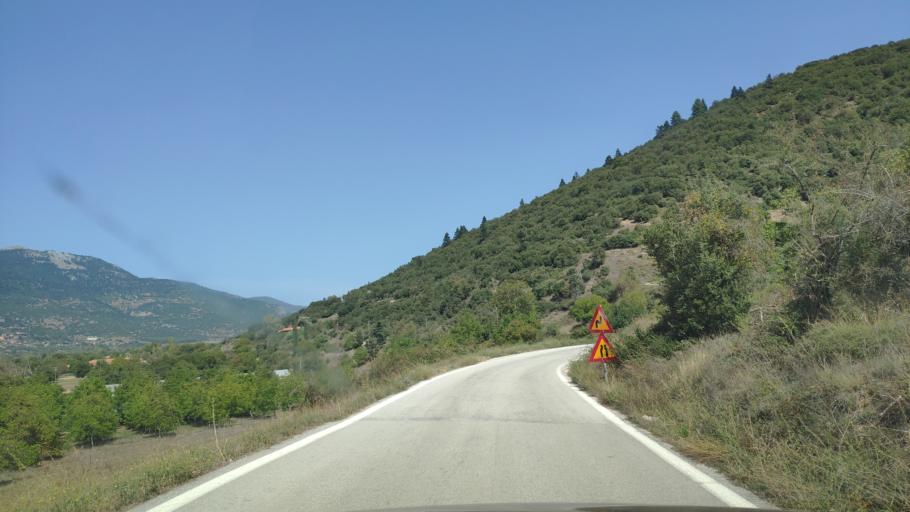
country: GR
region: West Greece
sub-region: Nomos Achaias
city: Aiyira
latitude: 37.9154
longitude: 22.3296
